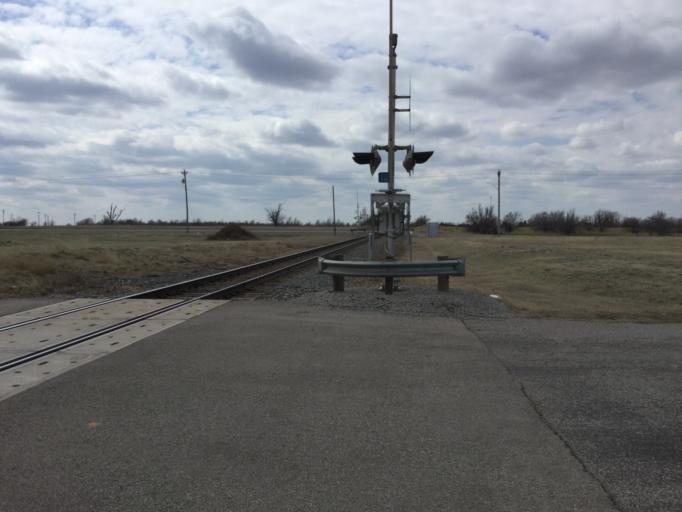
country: US
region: Kansas
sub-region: Kiowa County
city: Greensburg
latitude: 37.6094
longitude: -99.2968
